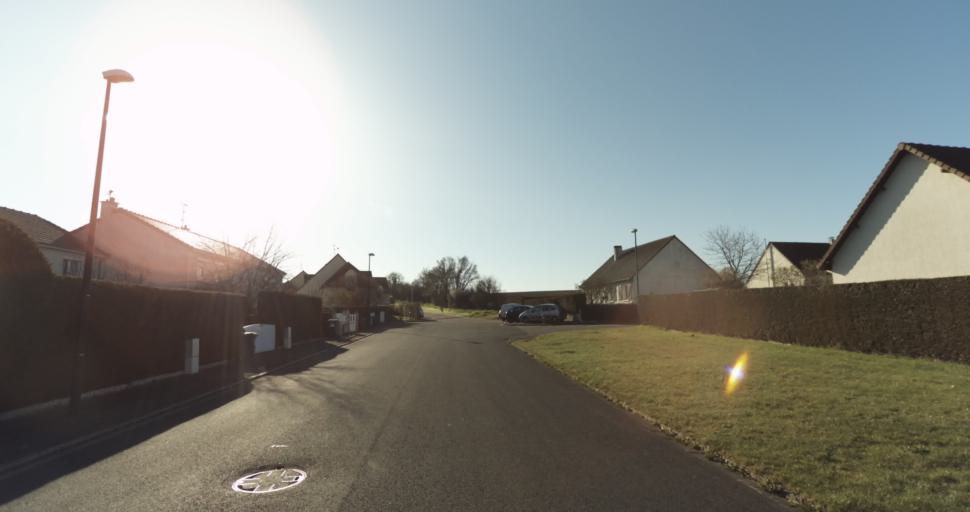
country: FR
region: Lower Normandy
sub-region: Departement du Calvados
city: Saint-Pierre-sur-Dives
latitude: 49.0220
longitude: -0.0259
